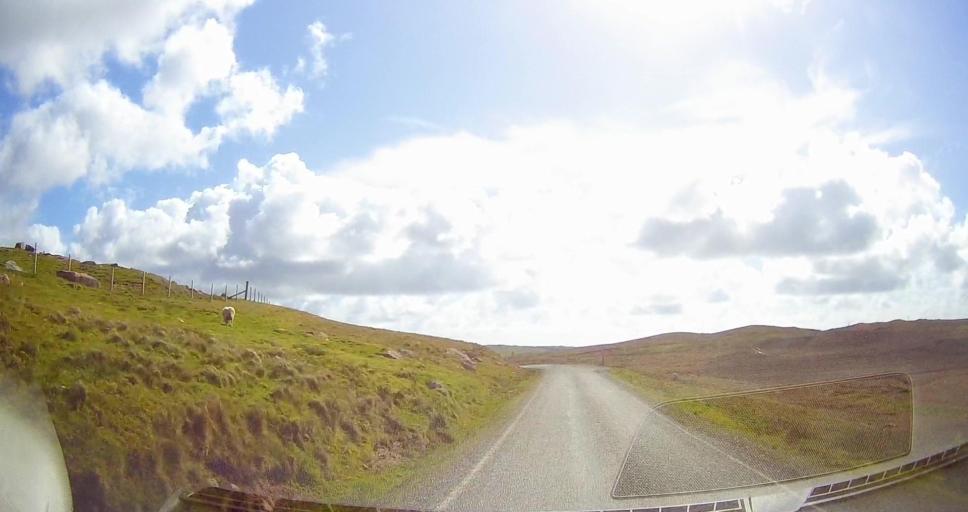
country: GB
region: Scotland
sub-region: Shetland Islands
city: Lerwick
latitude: 60.4834
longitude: -1.4036
